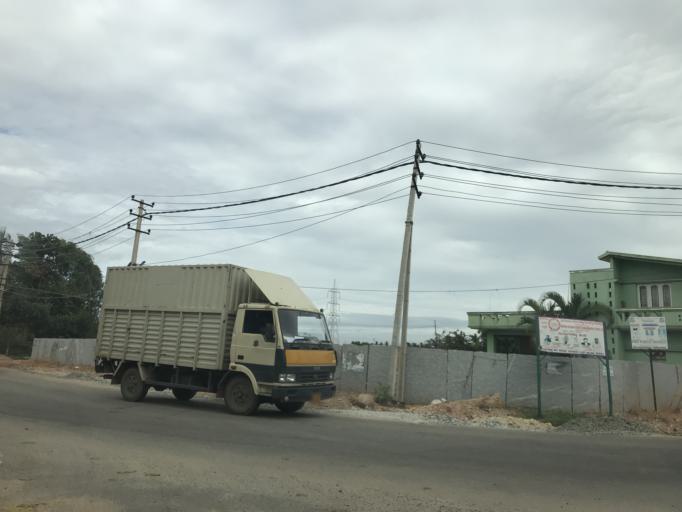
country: IN
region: Karnataka
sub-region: Bangalore Rural
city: Devanhalli
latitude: 13.1827
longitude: 77.6730
